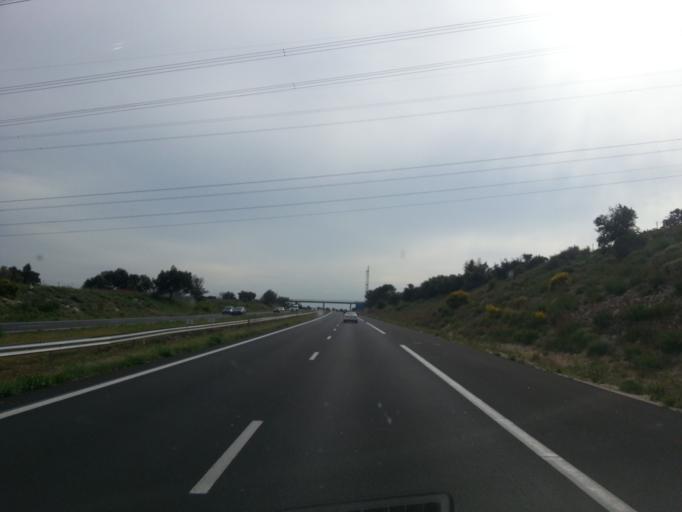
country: FR
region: Languedoc-Roussillon
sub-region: Departement du Gard
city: Rochefort-du-Gard
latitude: 43.9797
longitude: 4.6632
